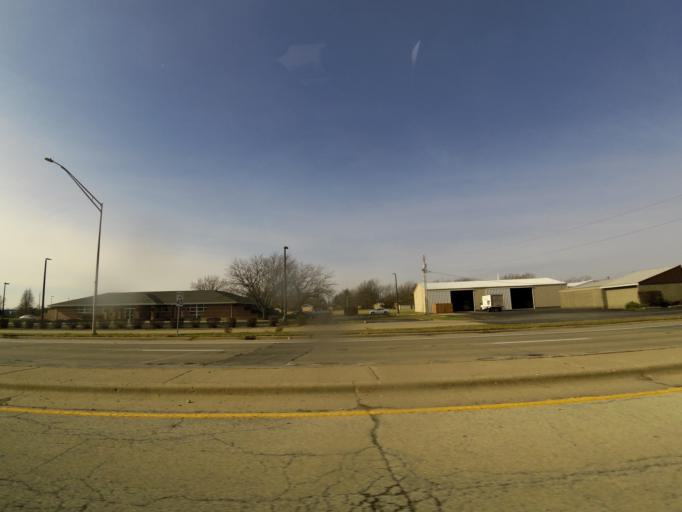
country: US
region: Illinois
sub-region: Macon County
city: Forsyth
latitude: 39.9335
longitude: -88.9556
